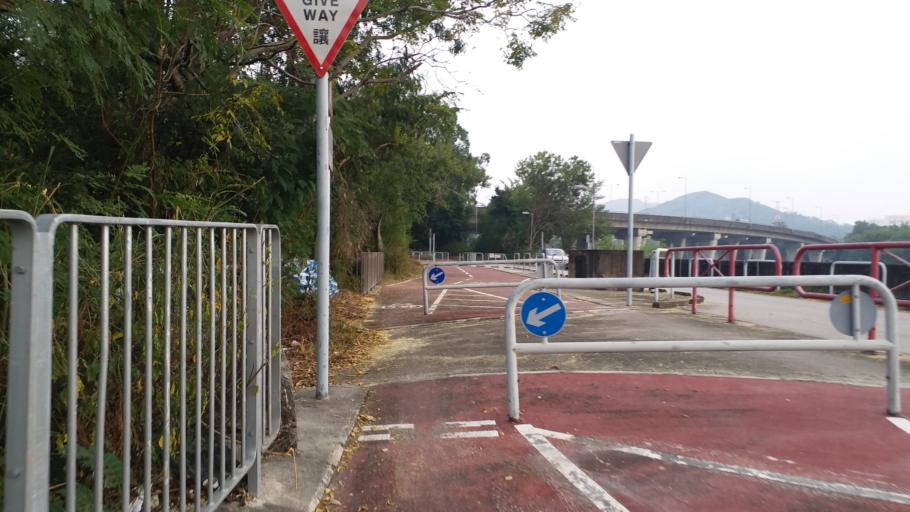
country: HK
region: Yuen Long
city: Yuen Long Kau Hui
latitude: 22.4550
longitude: 114.0488
